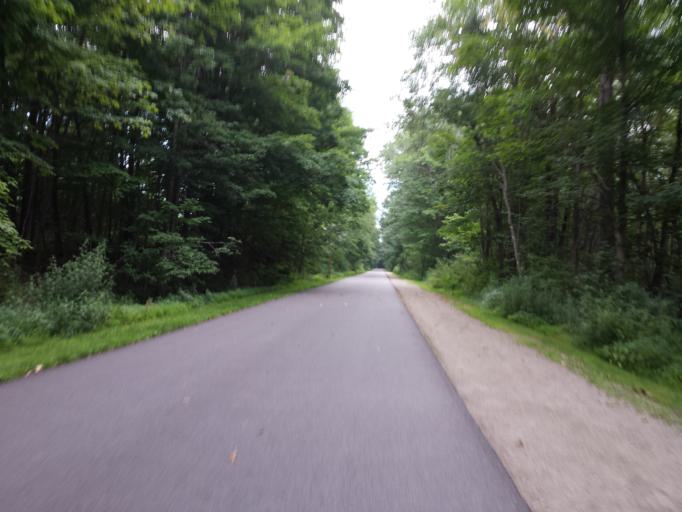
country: US
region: New York
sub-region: Dutchess County
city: Myers Corner
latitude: 41.6200
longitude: -73.8492
